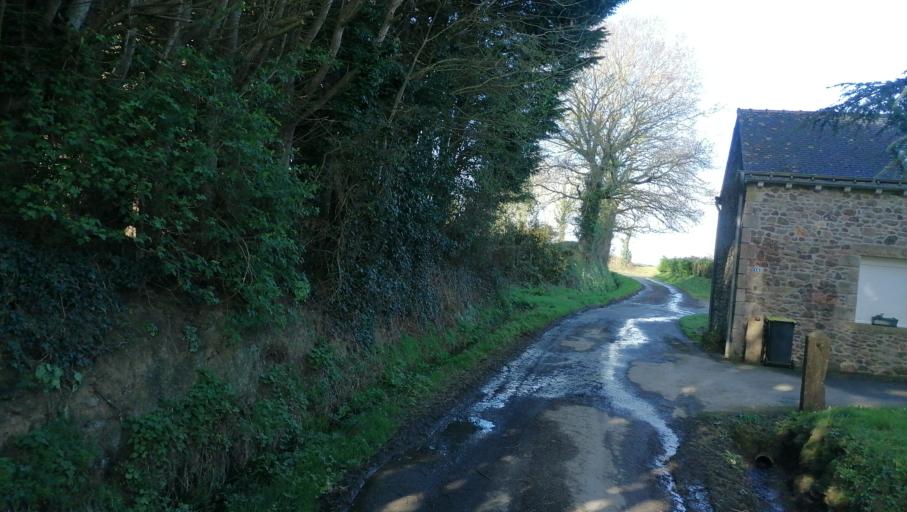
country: FR
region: Brittany
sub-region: Departement des Cotes-d'Armor
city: Pleguien
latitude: 48.6481
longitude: -2.9078
